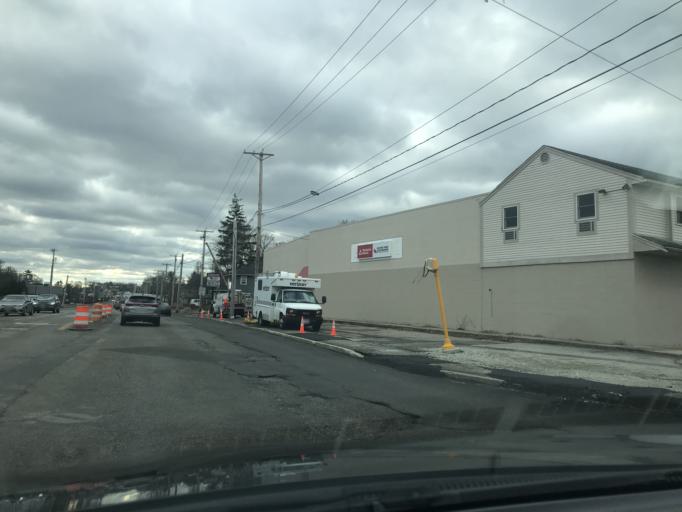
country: US
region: Massachusetts
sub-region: Plymouth County
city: Rockland
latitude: 42.1525
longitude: -70.9552
